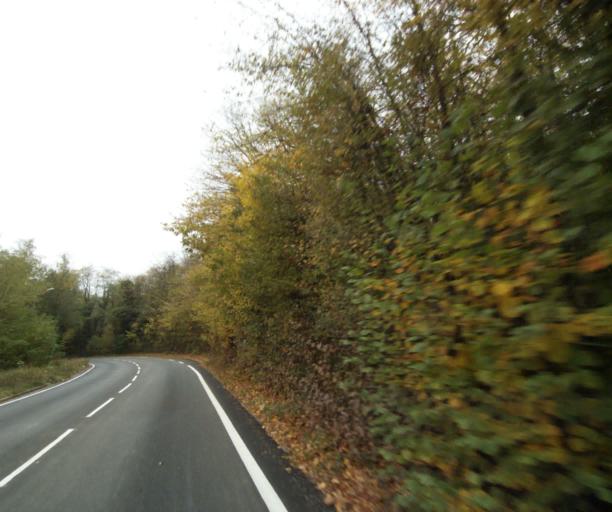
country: FR
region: Lorraine
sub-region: Departement de Meurthe-et-Moselle
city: Joeuf
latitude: 49.2337
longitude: 6.0265
